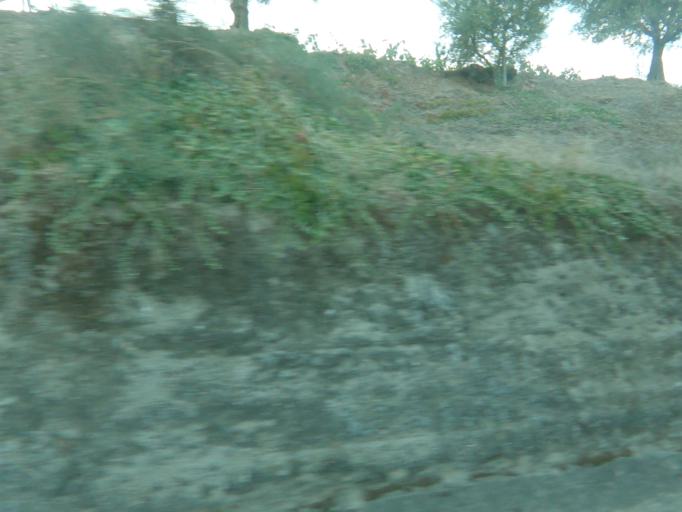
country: PT
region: Vila Real
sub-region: Peso da Regua
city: Godim
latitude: 41.1659
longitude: -7.8098
